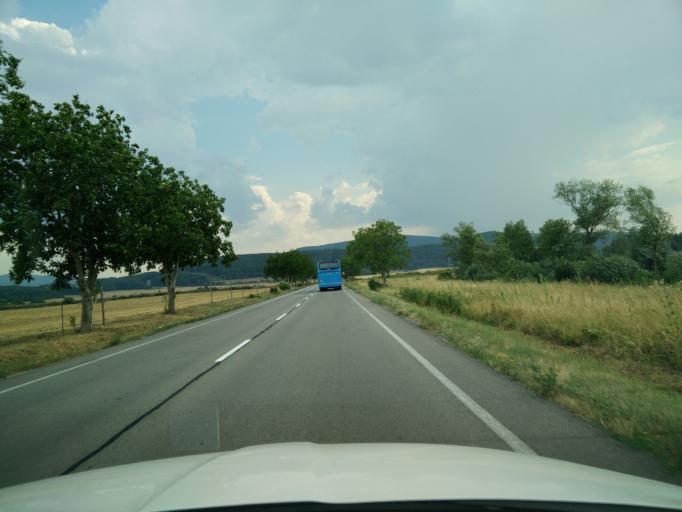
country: SK
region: Nitriansky
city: Novaky
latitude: 48.7360
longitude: 18.5012
